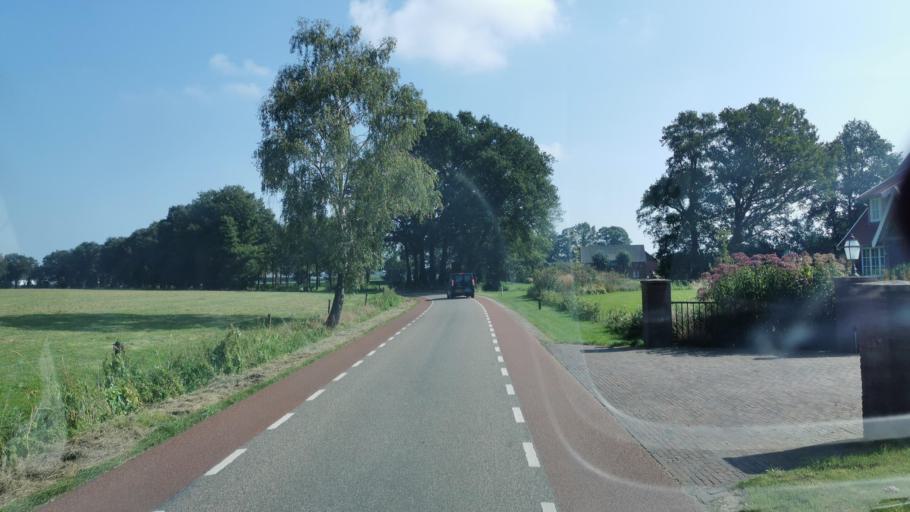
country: NL
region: Overijssel
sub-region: Gemeente Tubbergen
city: Tubbergen
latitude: 52.3490
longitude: 6.8234
